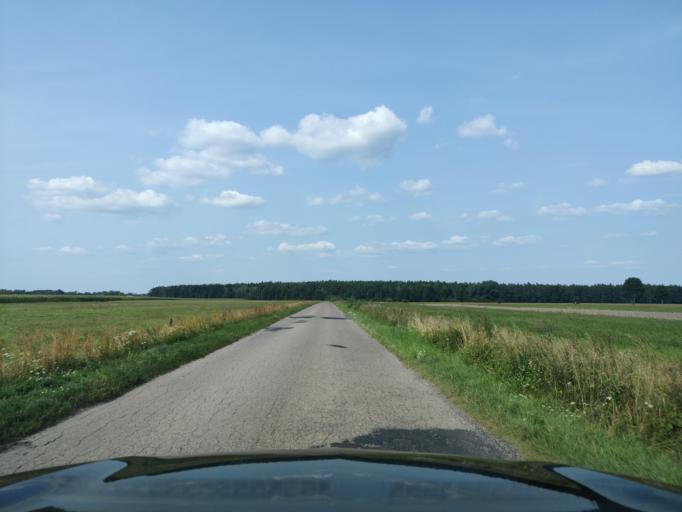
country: PL
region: Masovian Voivodeship
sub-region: Powiat wyszkowski
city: Rzasnik
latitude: 52.7461
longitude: 21.3190
